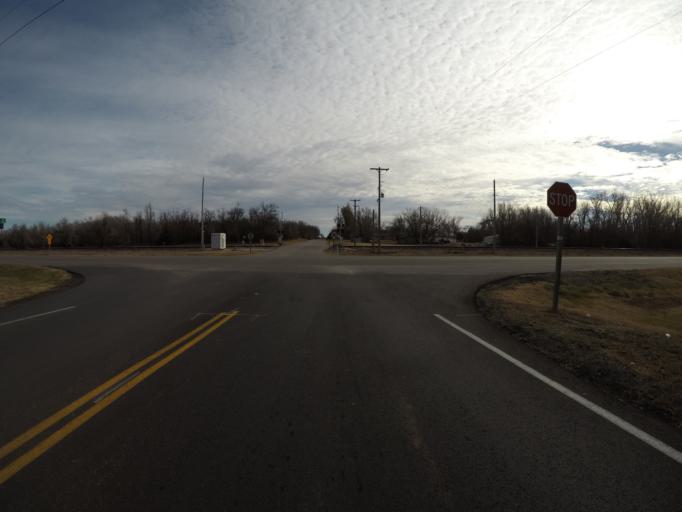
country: US
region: Kansas
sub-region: Reno County
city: Hutchinson
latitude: 38.1156
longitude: -97.8646
